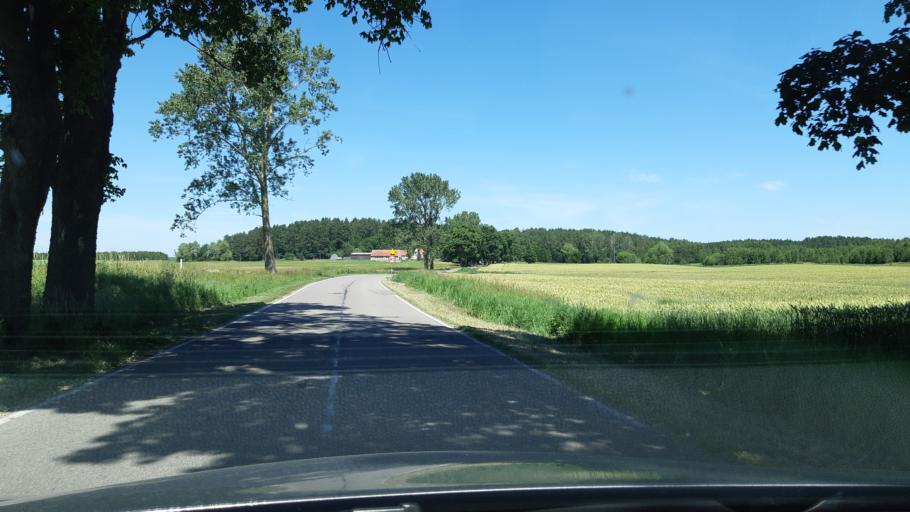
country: PL
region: Warmian-Masurian Voivodeship
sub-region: Powiat mragowski
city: Mikolajki
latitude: 53.8754
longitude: 21.6532
